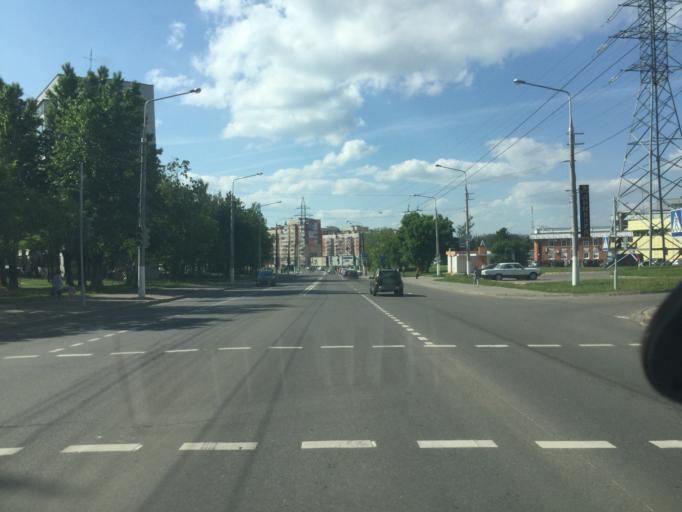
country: BY
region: Vitebsk
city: Vitebsk
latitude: 55.1835
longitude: 30.2340
